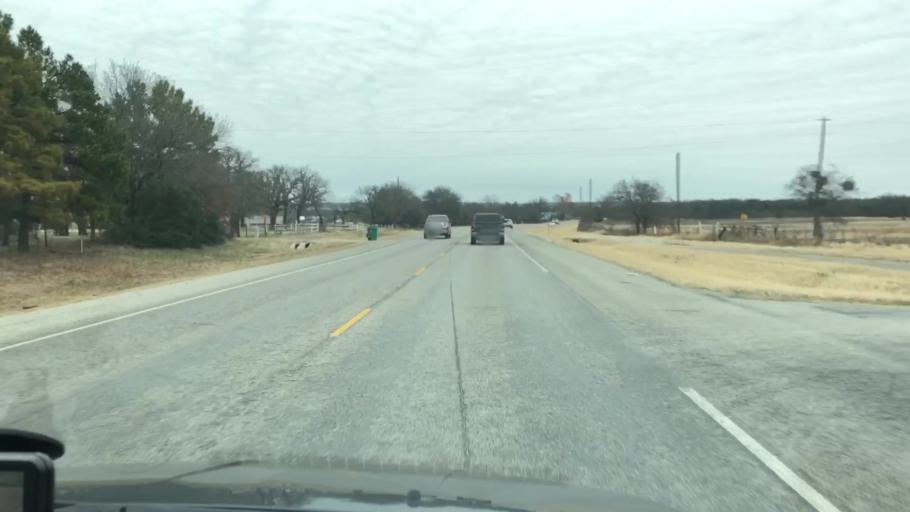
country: US
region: Texas
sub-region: Palo Pinto County
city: Mineral Wells
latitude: 32.8888
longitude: -98.0883
